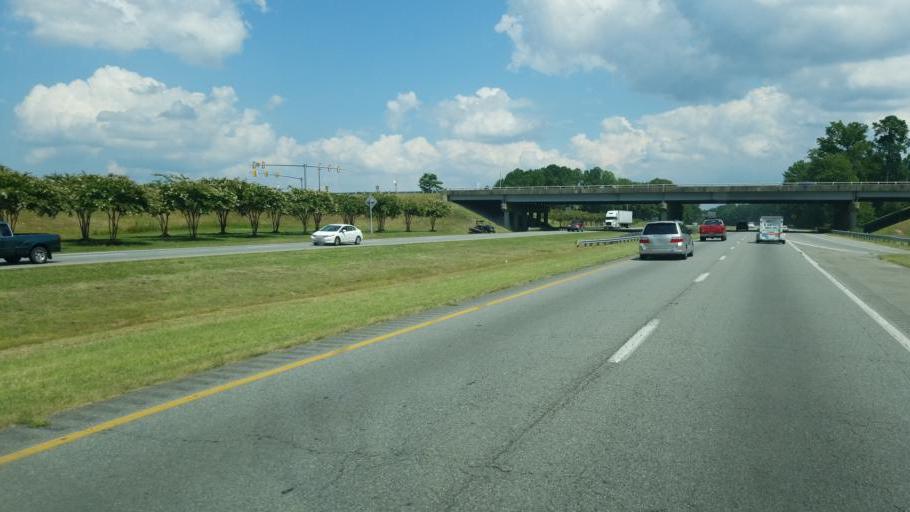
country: US
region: Virginia
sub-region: City of Suffolk
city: Suffolk
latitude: 36.7672
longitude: -76.5873
